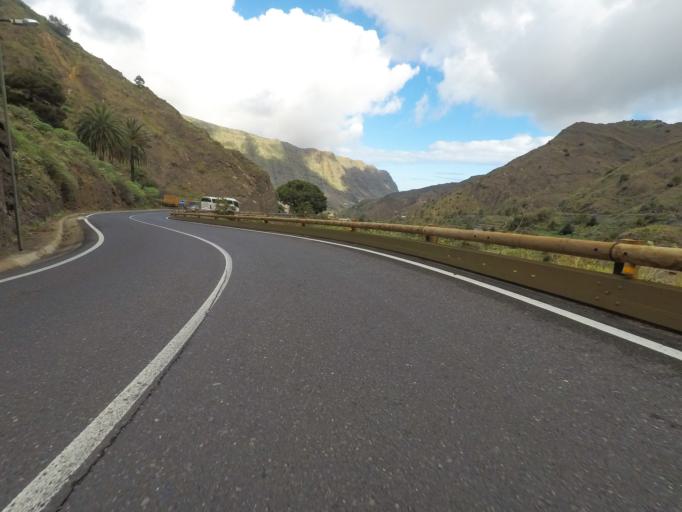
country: ES
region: Canary Islands
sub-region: Provincia de Santa Cruz de Tenerife
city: Hermigua
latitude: 28.1449
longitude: -17.1975
